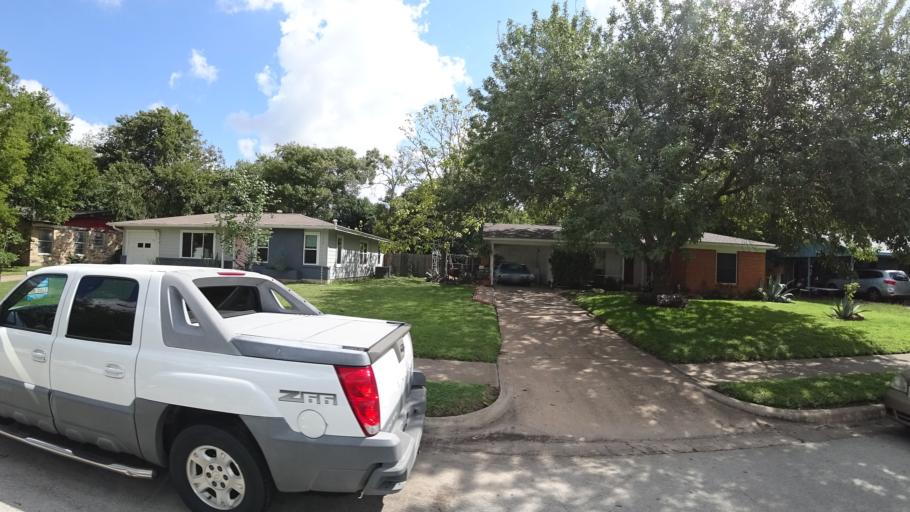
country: US
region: Texas
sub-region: Travis County
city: Austin
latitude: 30.3577
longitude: -97.7211
